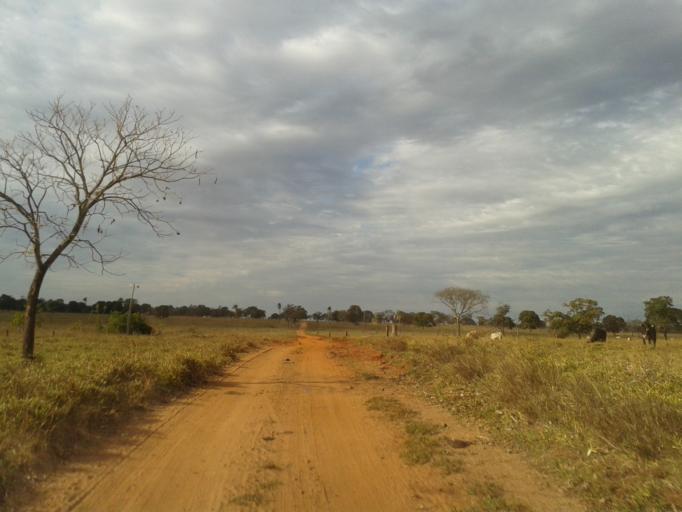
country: BR
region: Minas Gerais
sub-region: Santa Vitoria
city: Santa Vitoria
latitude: -18.7454
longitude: -50.2095
